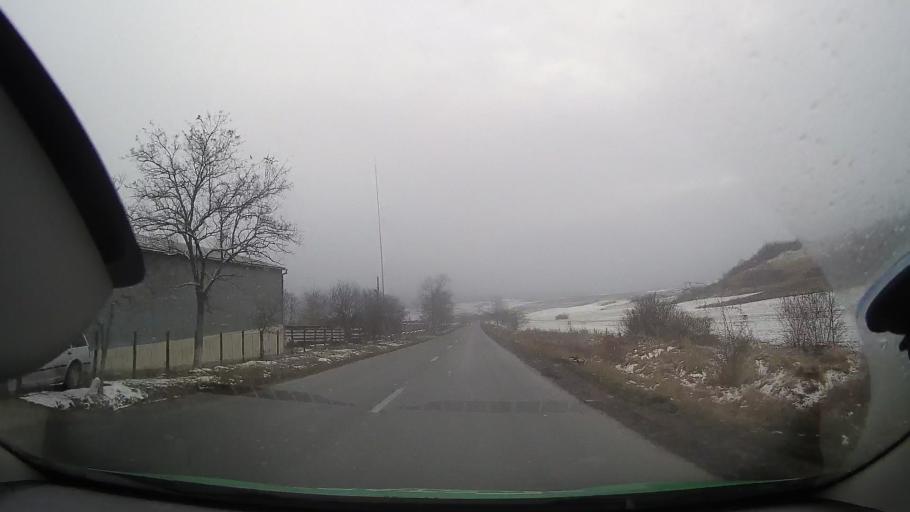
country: RO
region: Sibiu
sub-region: Comuna Blajel
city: Blajel
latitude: 46.2519
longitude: 24.2999
